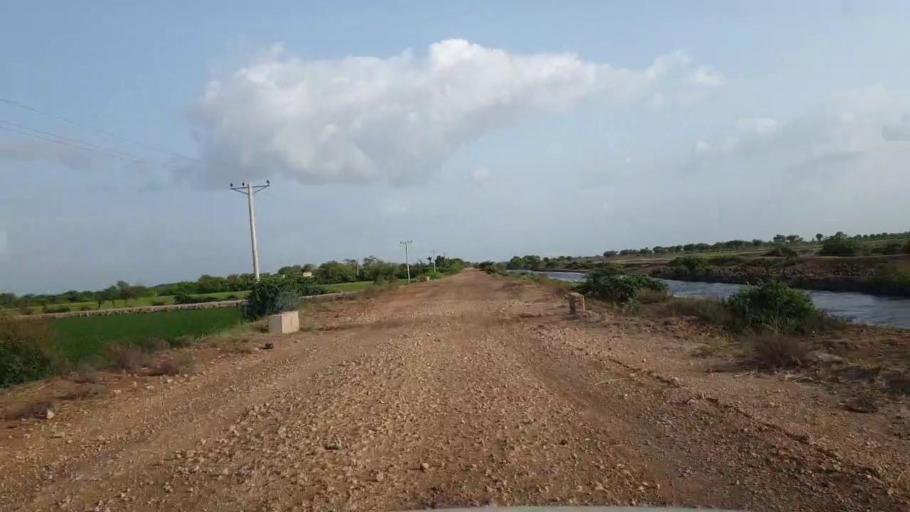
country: PK
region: Sindh
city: Kario
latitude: 24.8140
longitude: 68.6468
